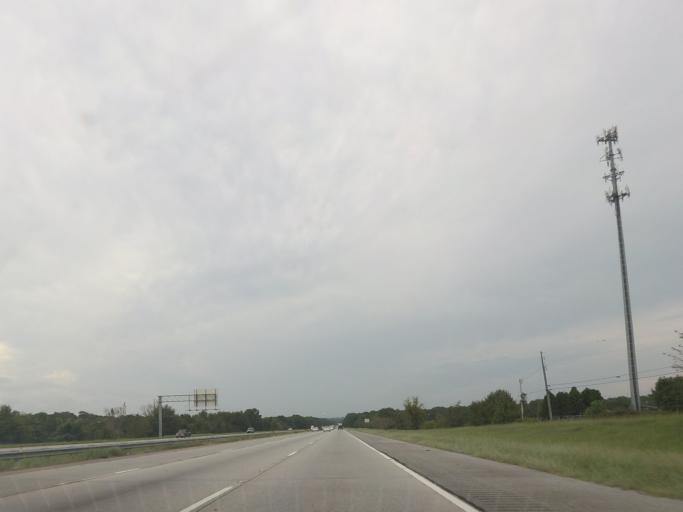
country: US
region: Georgia
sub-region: Bibb County
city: Macon
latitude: 32.7781
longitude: -83.6838
